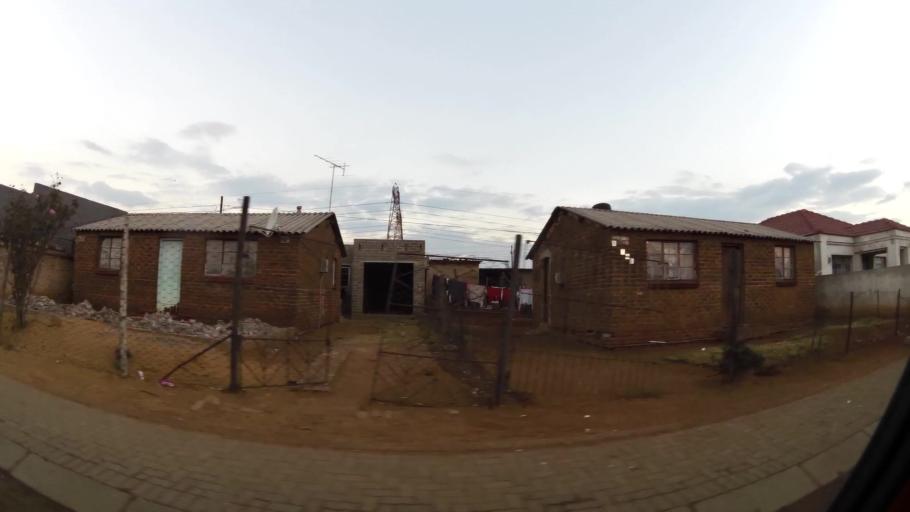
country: ZA
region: Gauteng
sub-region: City of Johannesburg Metropolitan Municipality
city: Orange Farm
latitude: -26.5581
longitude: 27.8649
